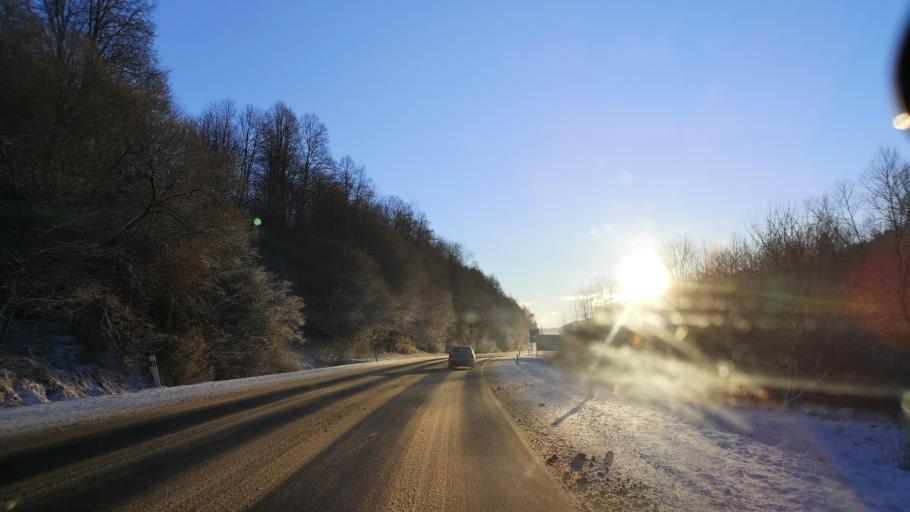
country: SK
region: Banskobystricky
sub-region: Okres Banska Bystrica
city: Brezno
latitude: 48.8115
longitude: 19.6046
